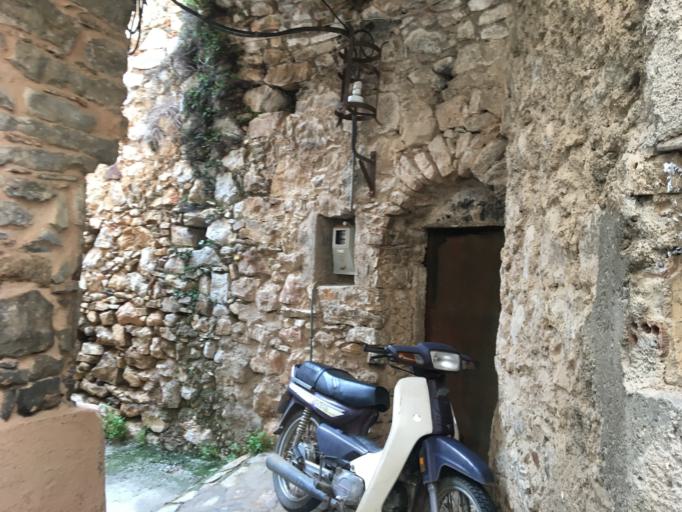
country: GR
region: North Aegean
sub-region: Chios
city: Thymiana
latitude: 38.2463
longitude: 25.9420
